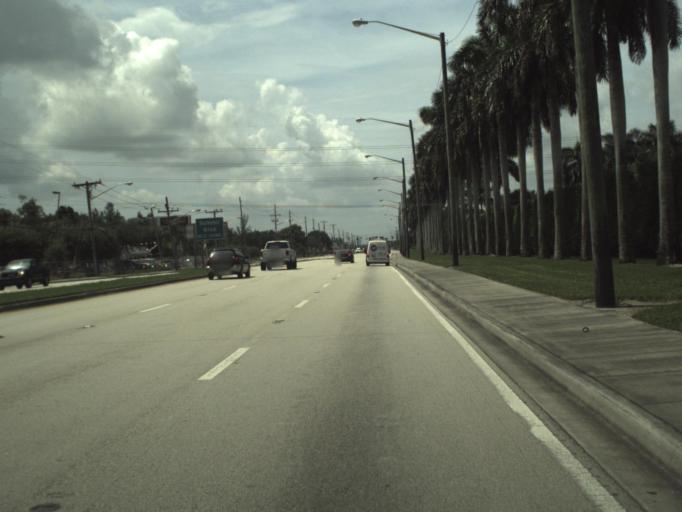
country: US
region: Florida
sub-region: Palm Beach County
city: Lake Clarke Shores
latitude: 26.6704
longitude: -80.0880
